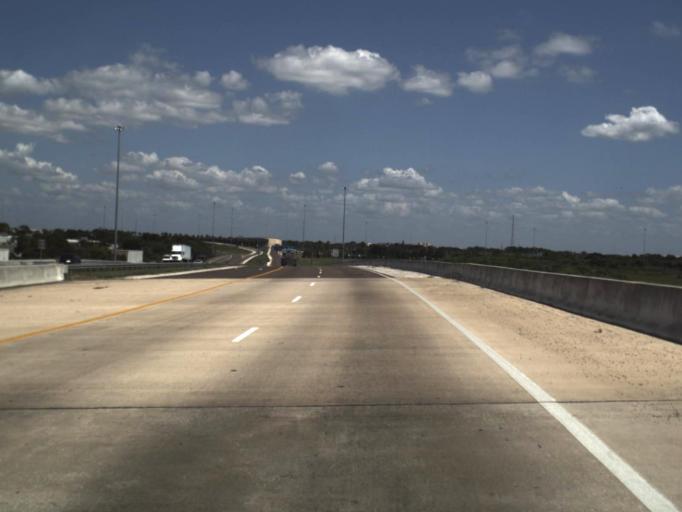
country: US
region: Florida
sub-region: Pinellas County
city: Feather Sound
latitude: 27.8771
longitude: -82.6719
